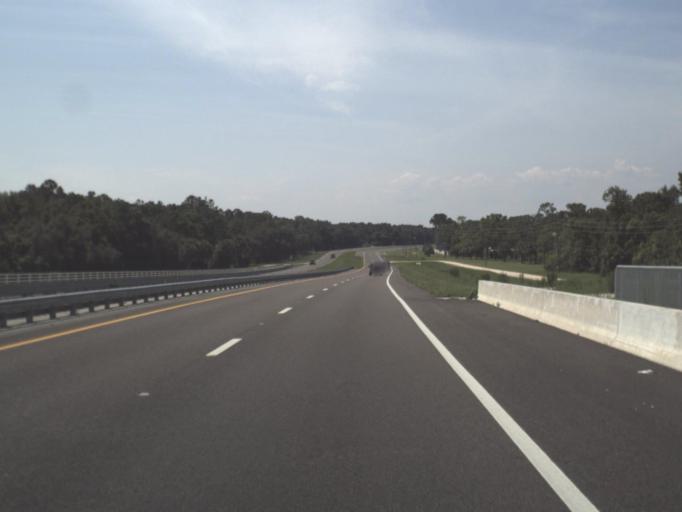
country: US
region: Florida
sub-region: Levy County
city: Inglis
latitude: 29.0149
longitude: -82.6649
